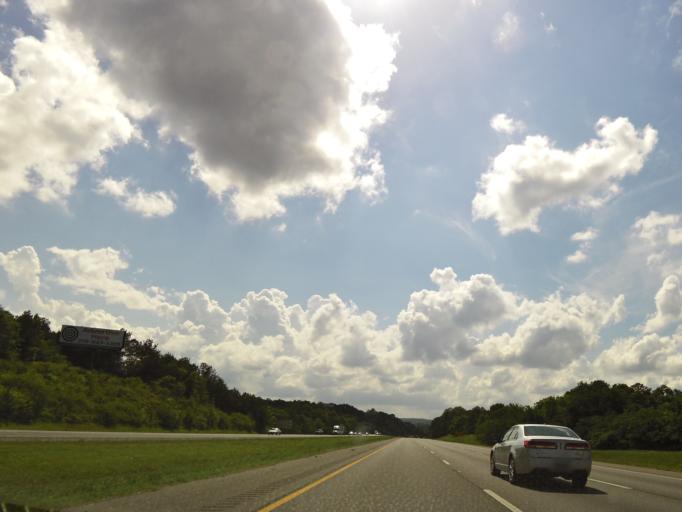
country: US
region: Alabama
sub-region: Jefferson County
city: Leeds
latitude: 33.5435
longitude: -86.6054
